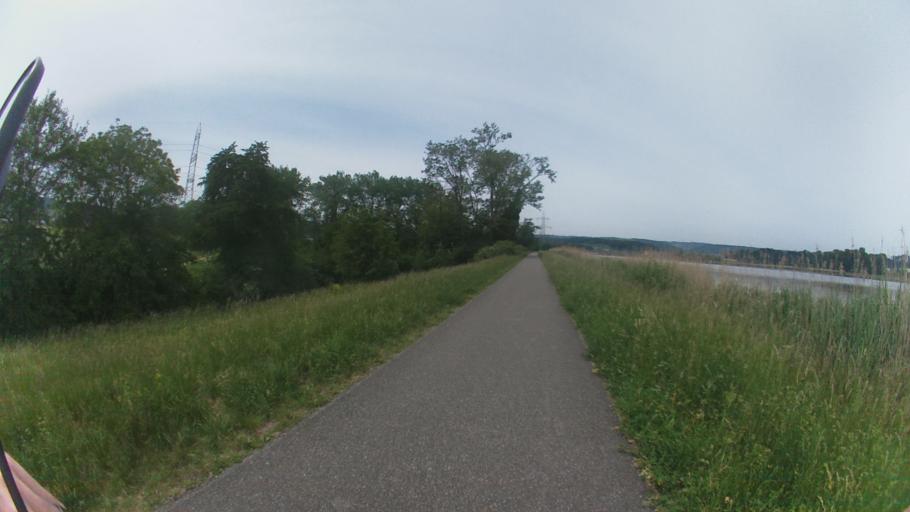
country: CH
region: Aargau
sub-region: Bezirk Zurzach
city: Klingnau
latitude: 47.5855
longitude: 8.2309
